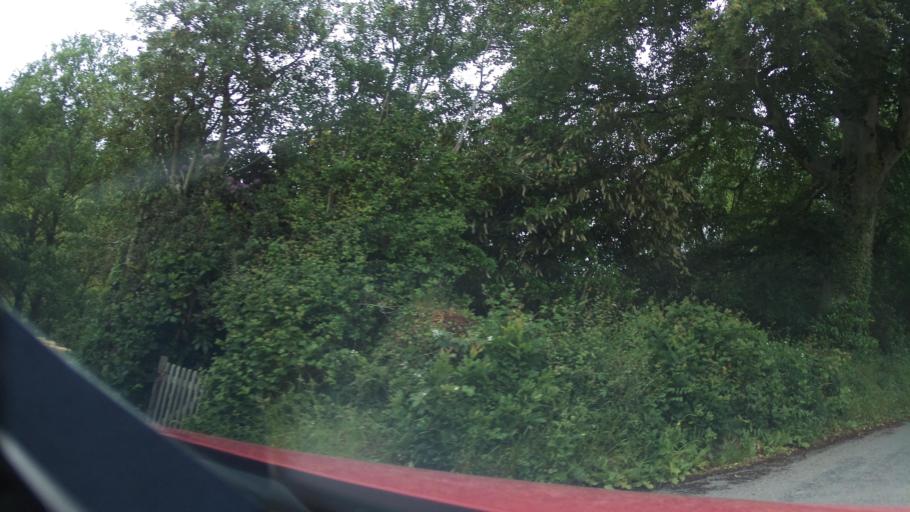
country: GB
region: England
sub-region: Devon
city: Crediton
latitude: 50.6979
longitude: -3.6335
